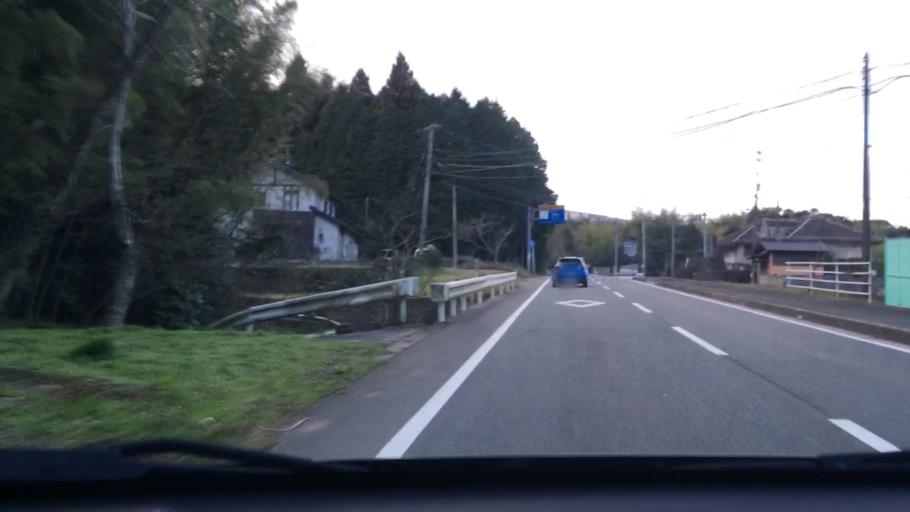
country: JP
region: Oita
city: Hiji
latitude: 33.3730
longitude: 131.4593
